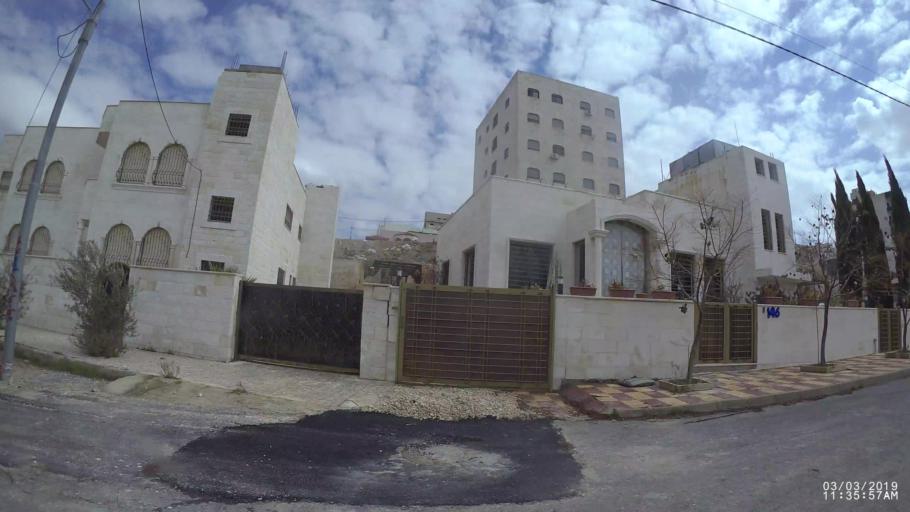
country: JO
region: Amman
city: Al Jubayhah
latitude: 32.0057
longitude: 35.9106
